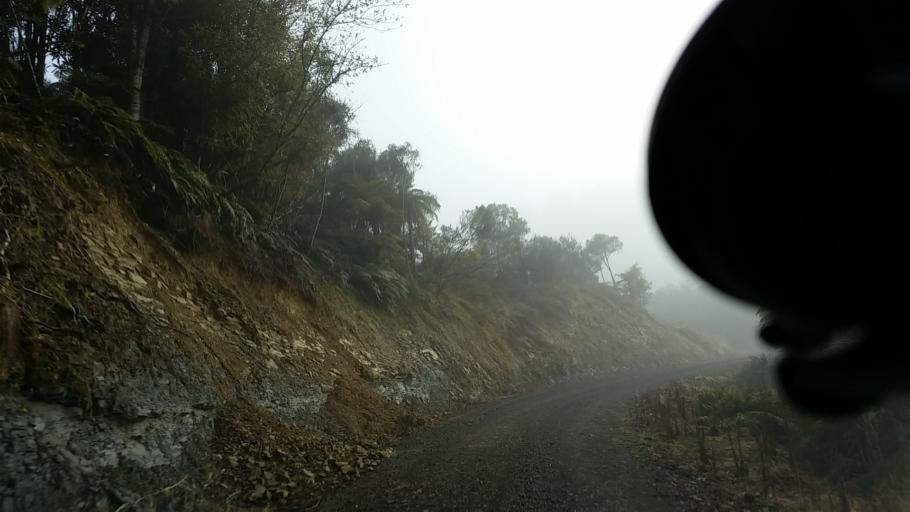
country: NZ
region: Taranaki
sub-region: New Plymouth District
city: Waitara
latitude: -38.9606
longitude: 174.7813
